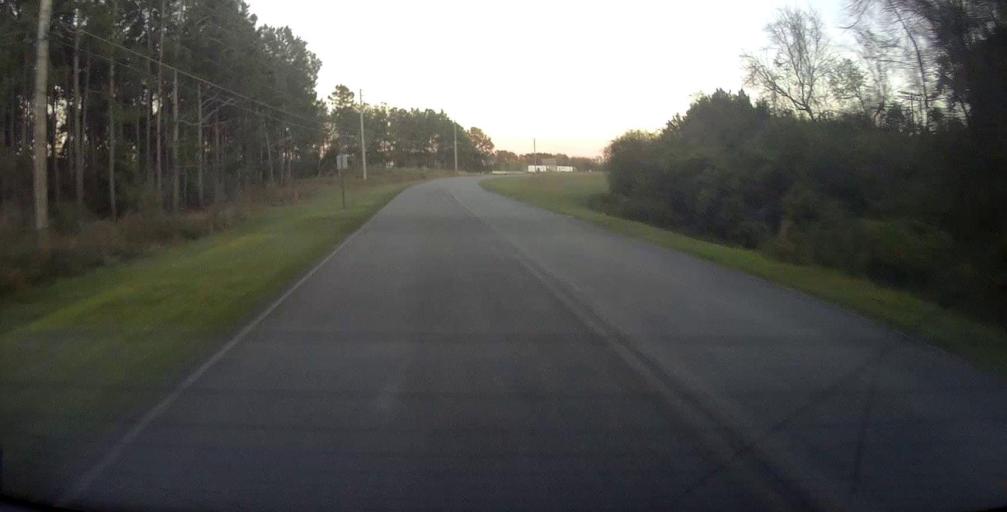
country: US
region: Georgia
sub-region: Crisp County
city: Cordele
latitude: 31.9509
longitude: -83.7520
